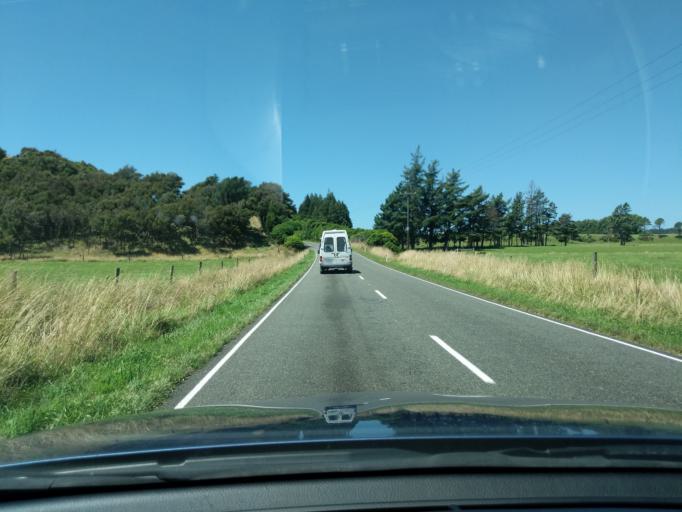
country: NZ
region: Tasman
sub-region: Tasman District
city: Takaka
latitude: -40.6940
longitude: 172.6379
